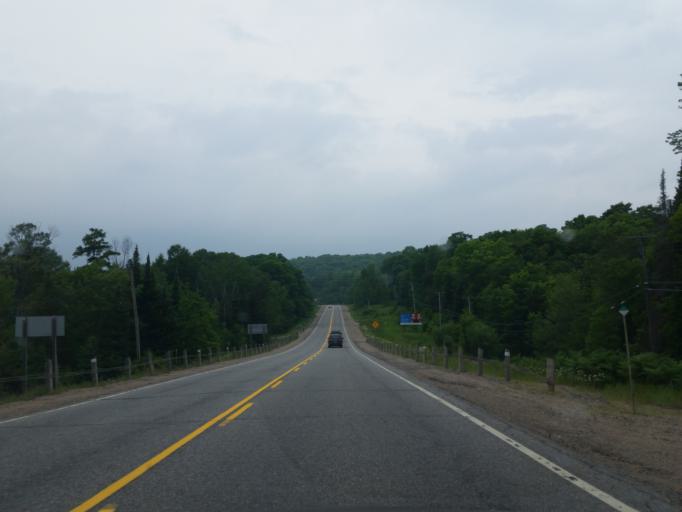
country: CA
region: Ontario
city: Huntsville
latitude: 45.3615
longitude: -79.1019
